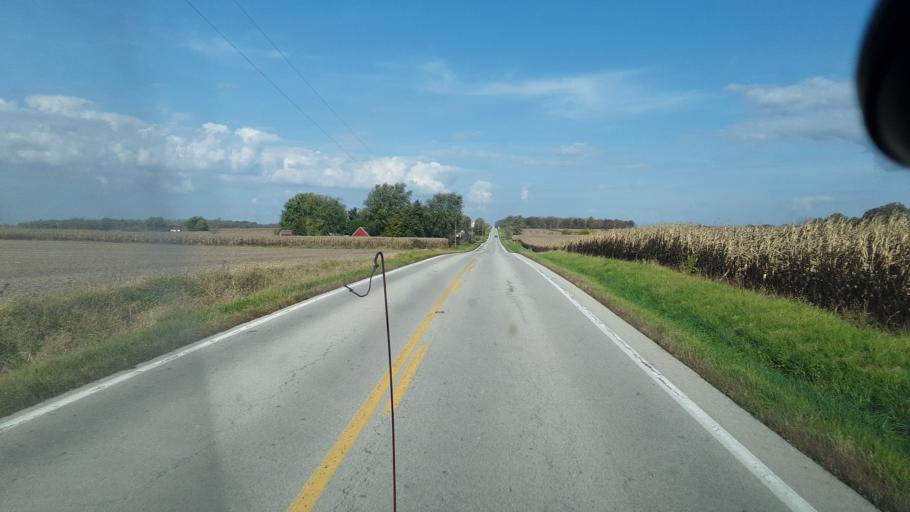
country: US
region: Ohio
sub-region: Clinton County
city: Sabina
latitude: 39.5223
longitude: -83.6964
